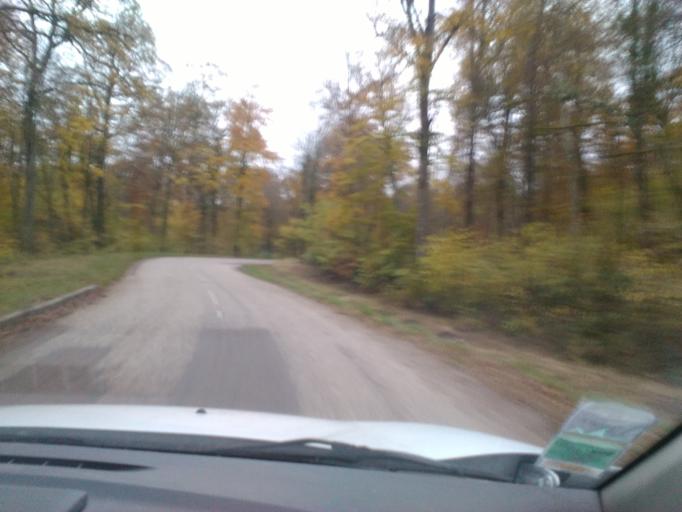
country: FR
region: Lorraine
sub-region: Departement des Vosges
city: Darnieulles
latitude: 48.2420
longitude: 6.2830
